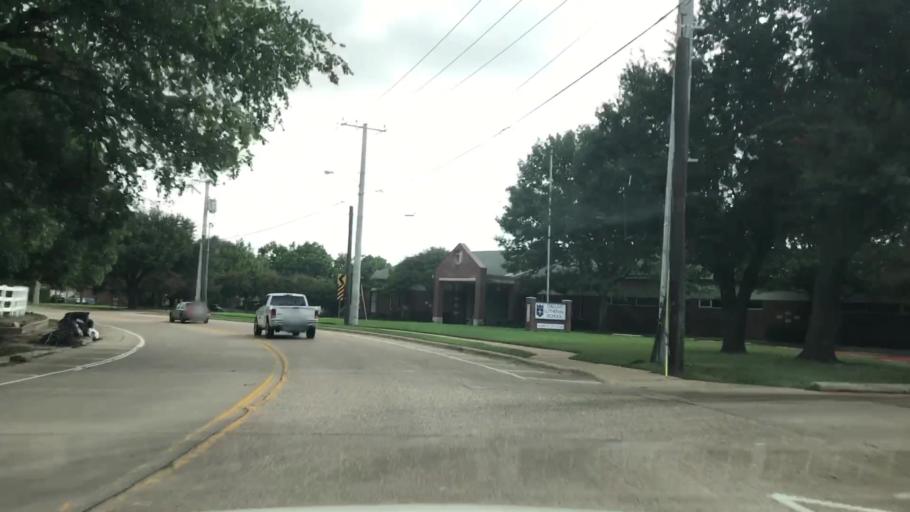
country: US
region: Texas
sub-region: Dallas County
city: Richardson
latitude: 32.9062
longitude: -96.7606
